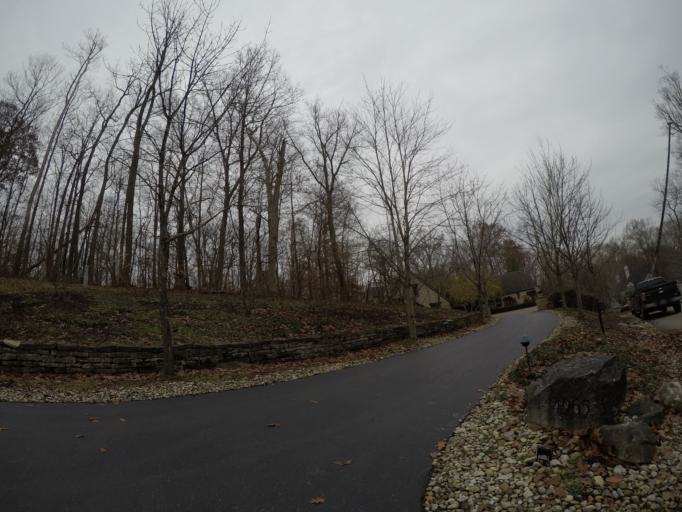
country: US
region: Ohio
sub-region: Franklin County
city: Dublin
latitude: 40.0536
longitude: -83.0907
